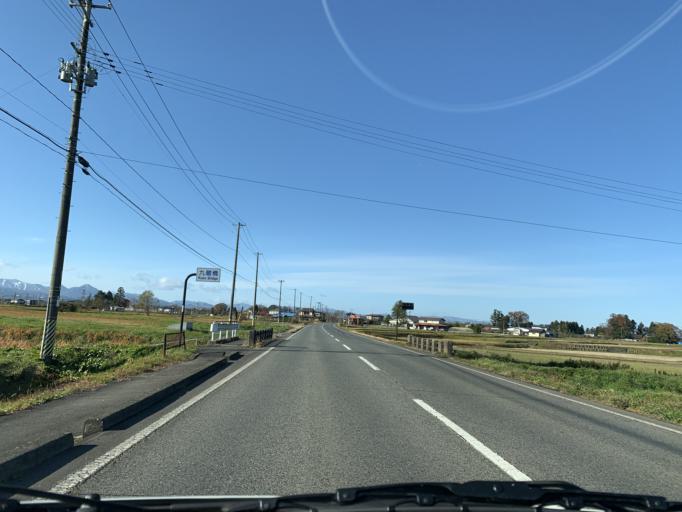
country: JP
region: Iwate
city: Mizusawa
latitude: 39.1796
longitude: 141.1336
